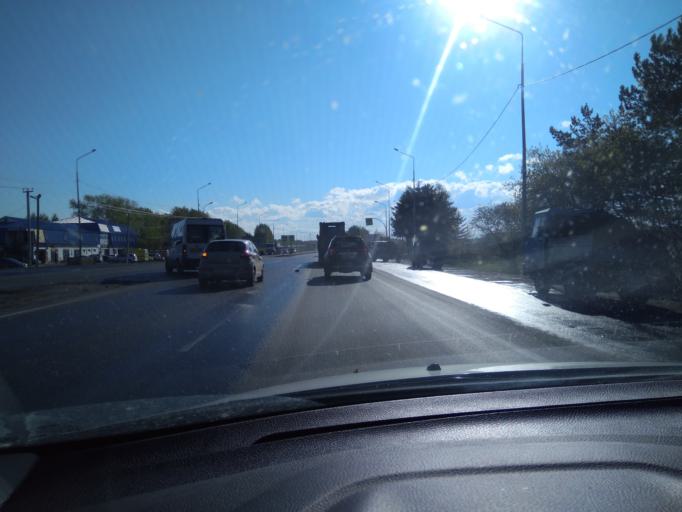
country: RU
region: Tjumen
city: Moskovskiy
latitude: 57.1198
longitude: 65.4439
